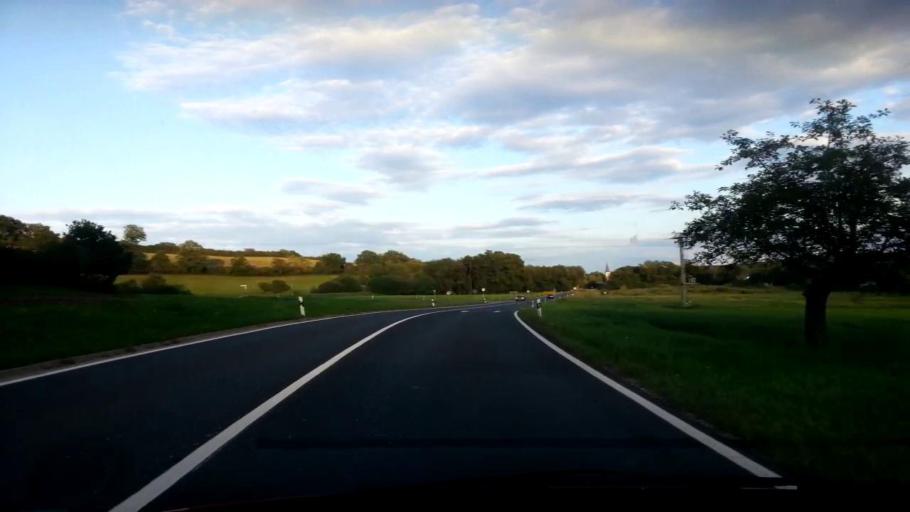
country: DE
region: Bavaria
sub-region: Upper Franconia
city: Burgwindheim
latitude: 49.8303
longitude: 10.5818
